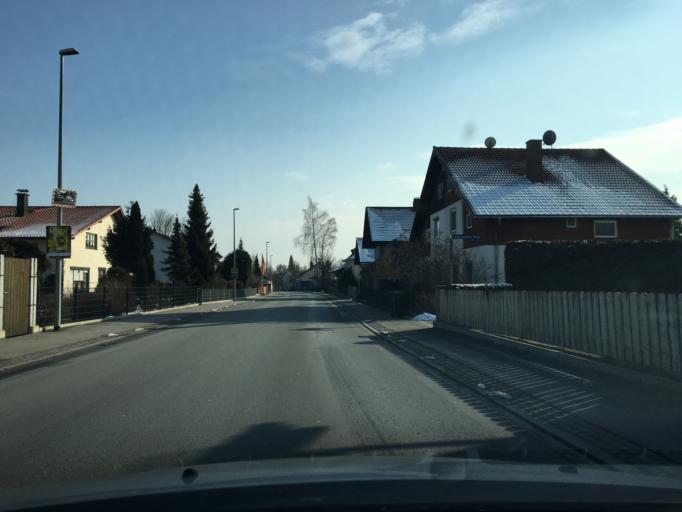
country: DE
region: Bavaria
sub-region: Lower Bavaria
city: Gangkofen
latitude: 48.4431
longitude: 12.5594
